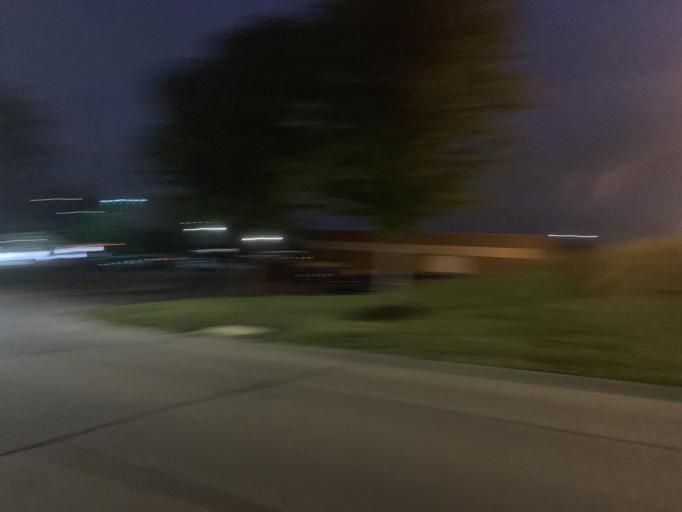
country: US
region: Nebraska
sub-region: Douglas County
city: Ralston
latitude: 41.1896
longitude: -96.0874
